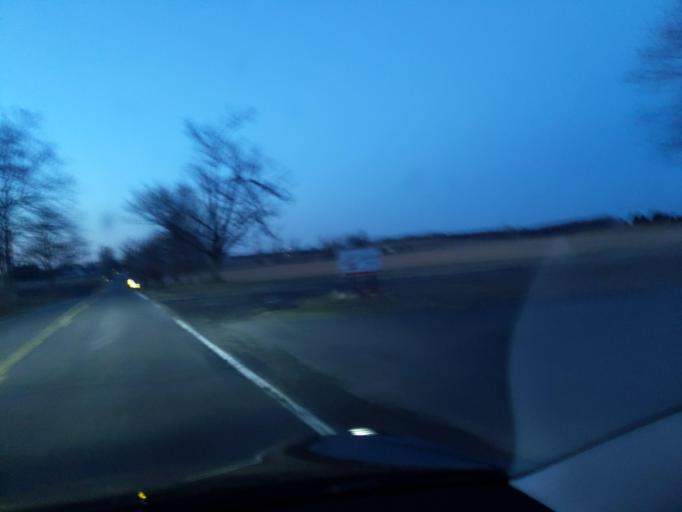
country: US
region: Michigan
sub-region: Ingham County
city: Stockbridge
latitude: 42.5379
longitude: -84.2210
